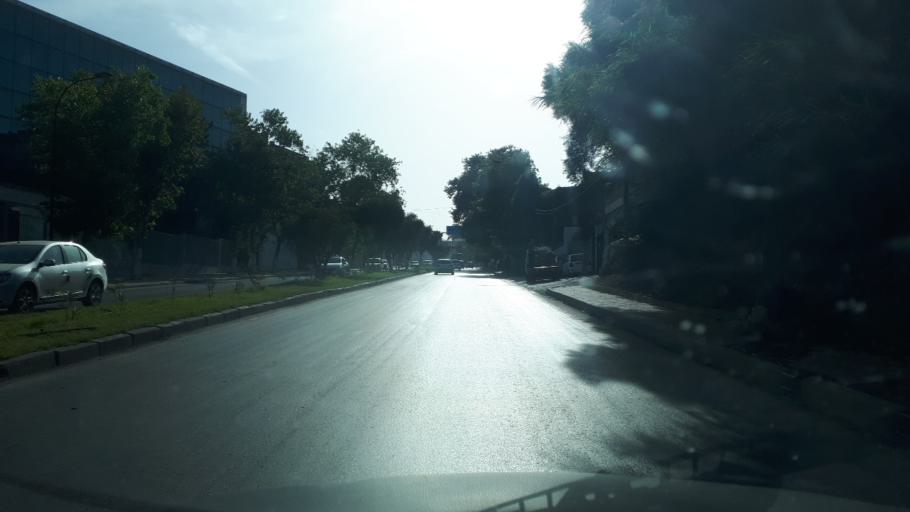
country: DZ
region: Alger
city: Algiers
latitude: 36.7710
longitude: 3.0154
